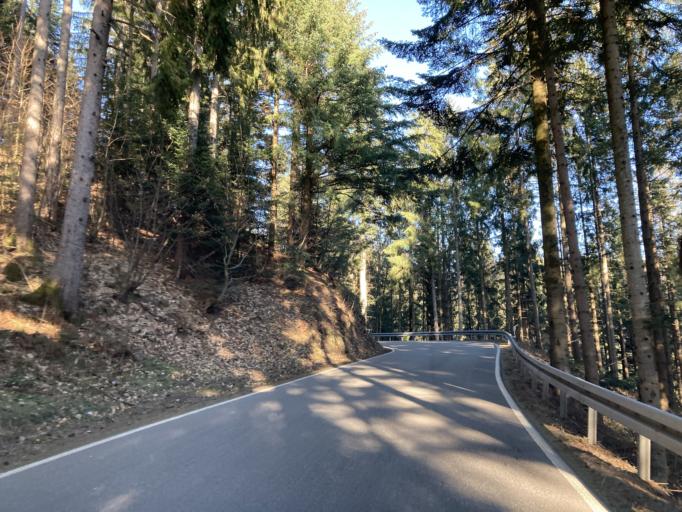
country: DE
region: Baden-Wuerttemberg
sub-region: Freiburg Region
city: Oppenau
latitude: 48.4853
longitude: 8.2073
